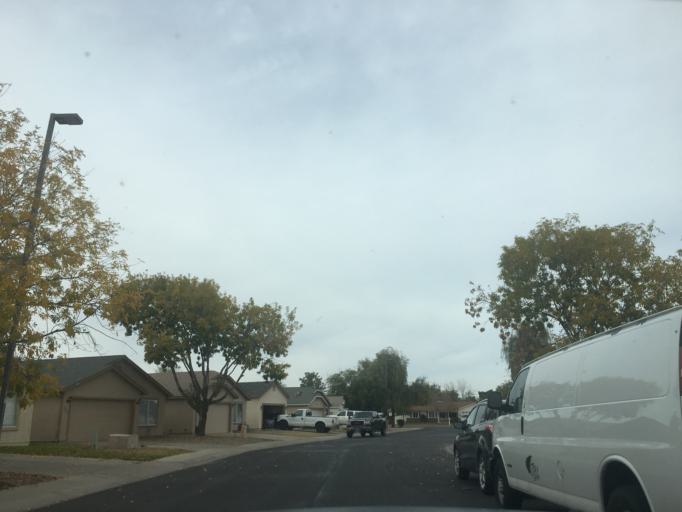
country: US
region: Arizona
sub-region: Maricopa County
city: Gilbert
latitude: 33.3581
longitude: -111.7868
